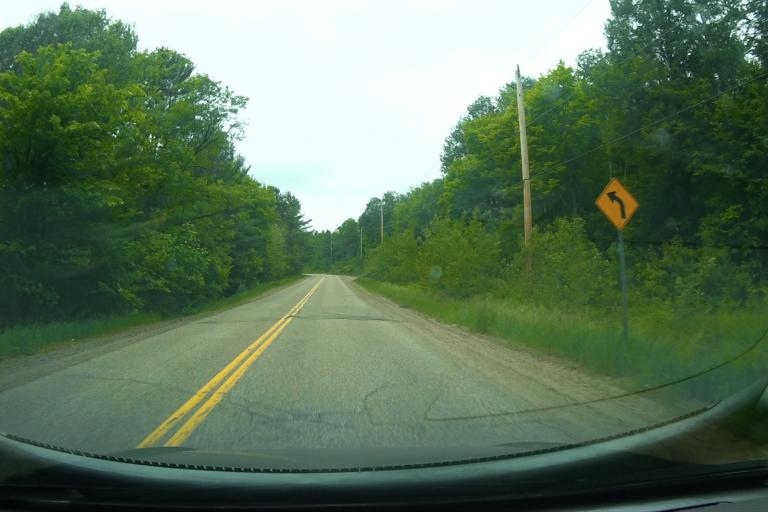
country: CA
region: Ontario
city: Pembroke
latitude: 45.4641
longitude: -77.2335
